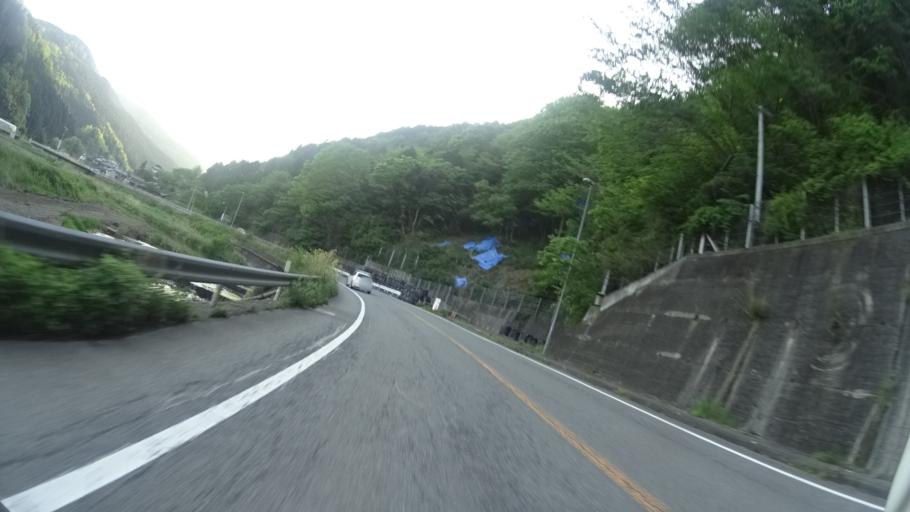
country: JP
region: Tokushima
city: Ikedacho
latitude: 34.0158
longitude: 133.7562
